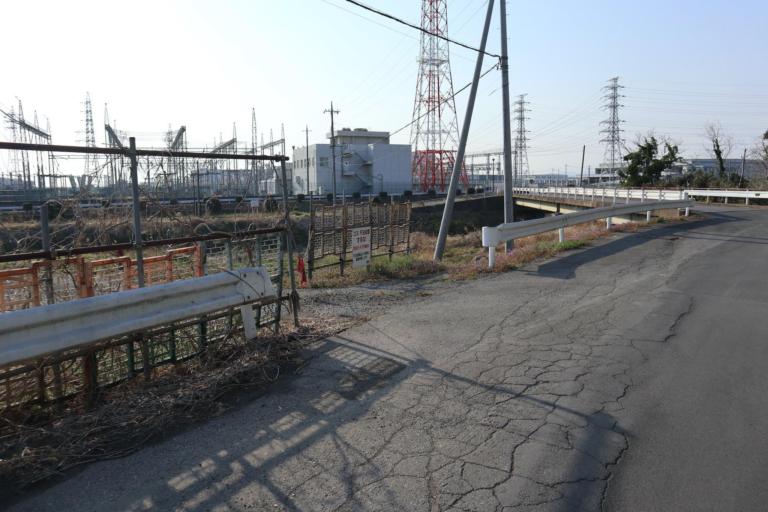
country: JP
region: Gunma
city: Tatebayashi
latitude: 36.2800
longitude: 139.5567
